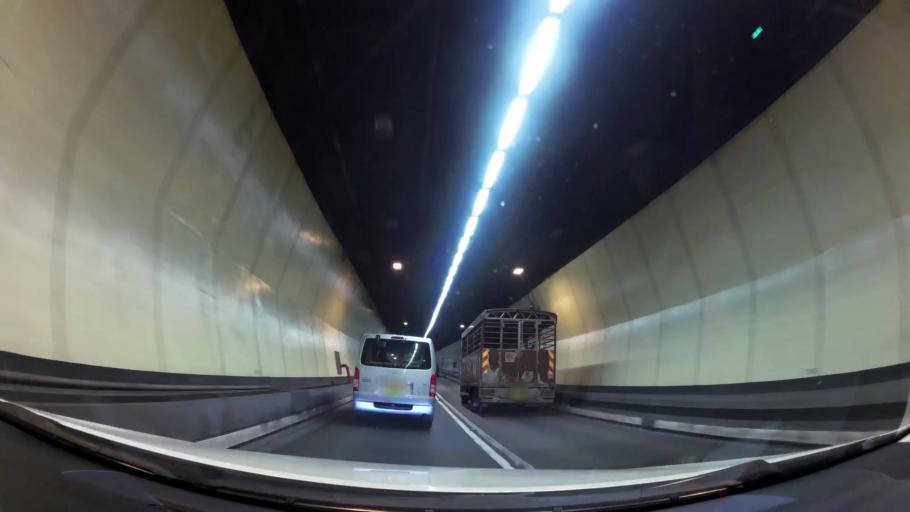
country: HK
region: Kowloon City
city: Kowloon
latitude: 22.2988
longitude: 114.1806
